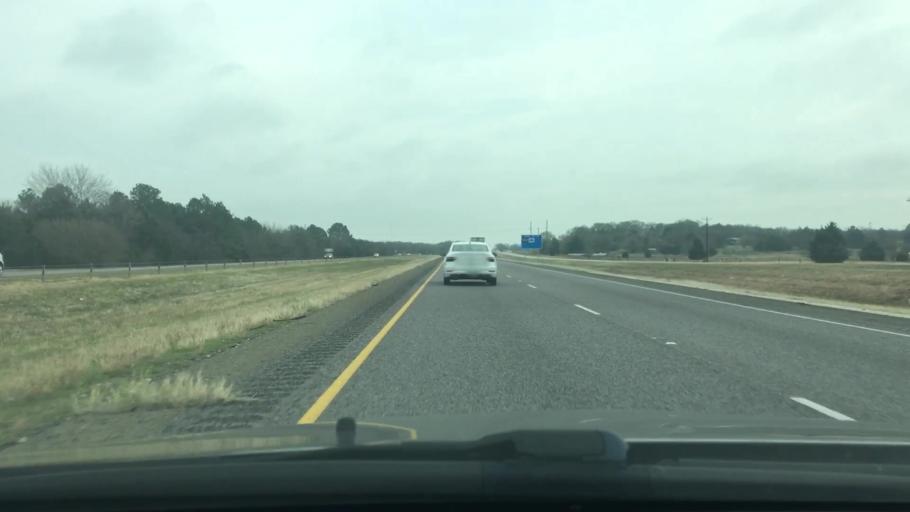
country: US
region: Texas
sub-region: Freestone County
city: Fairfield
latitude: 31.7392
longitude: -96.1892
